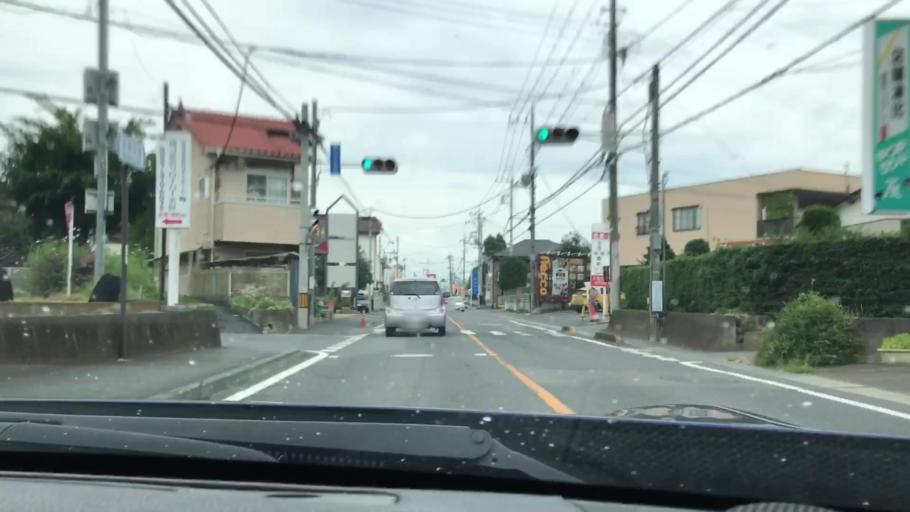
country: JP
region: Gunma
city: Takasaki
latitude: 36.3496
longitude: 139.0230
